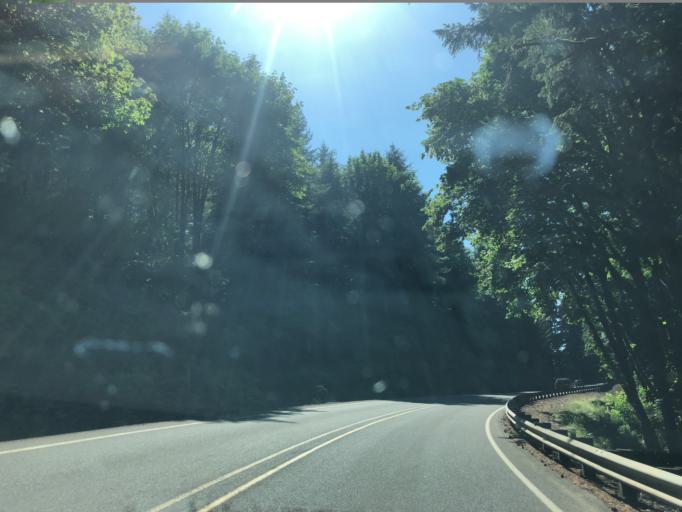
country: US
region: Oregon
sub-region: Linn County
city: Sweet Home
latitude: 44.4078
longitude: -122.5972
